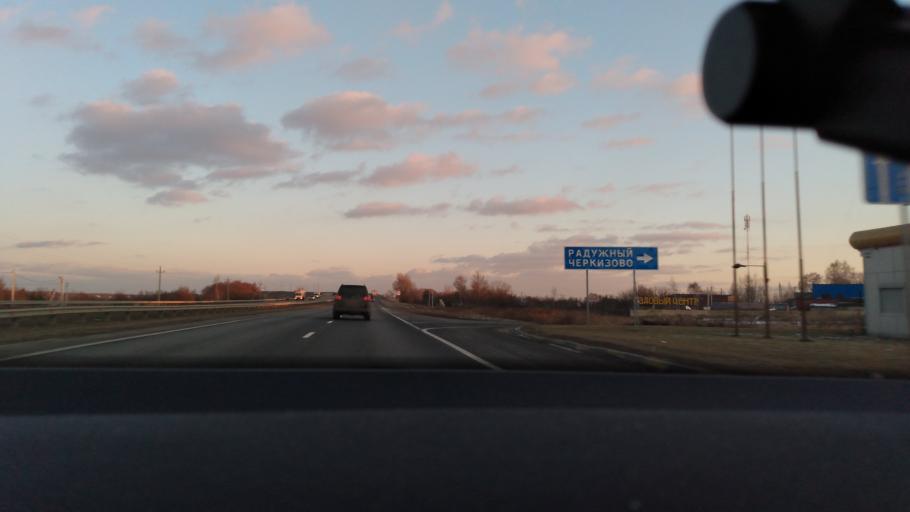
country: RU
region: Moskovskaya
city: Raduzhnyy
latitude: 55.1452
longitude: 38.7309
